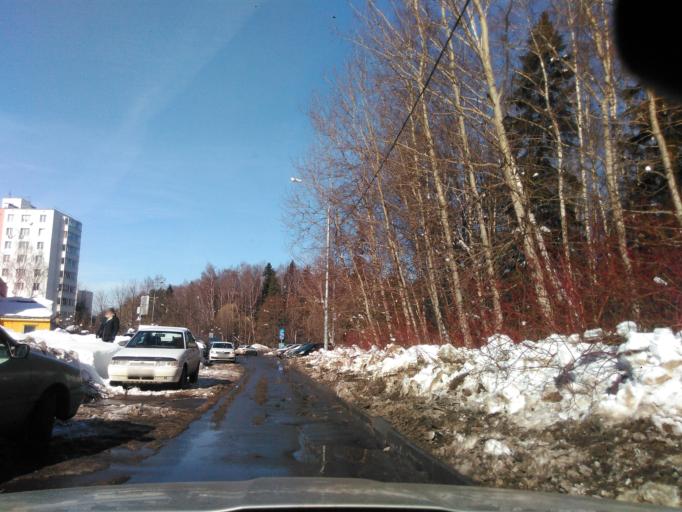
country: RU
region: Moscow
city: Zelenograd
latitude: 55.9795
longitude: 37.1941
